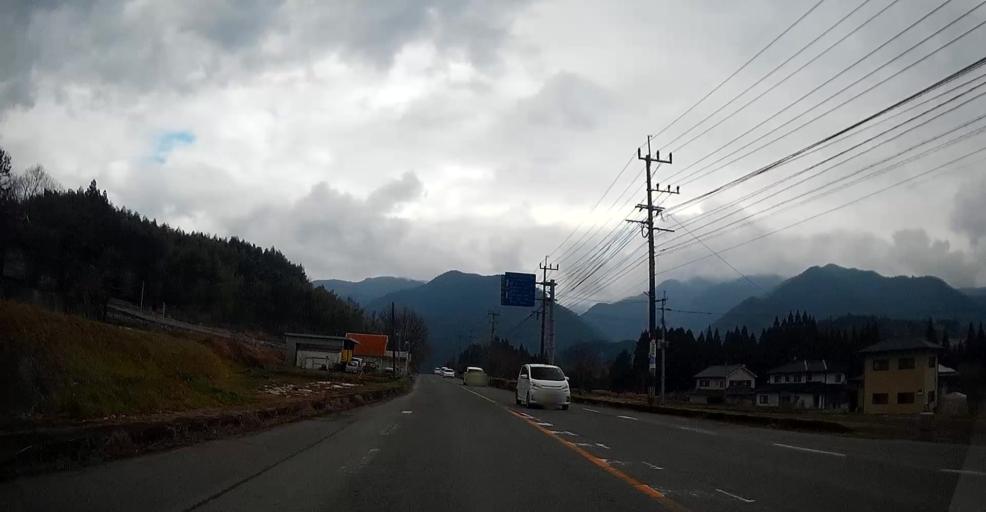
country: JP
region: Kumamoto
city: Matsubase
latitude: 32.6195
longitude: 130.8351
